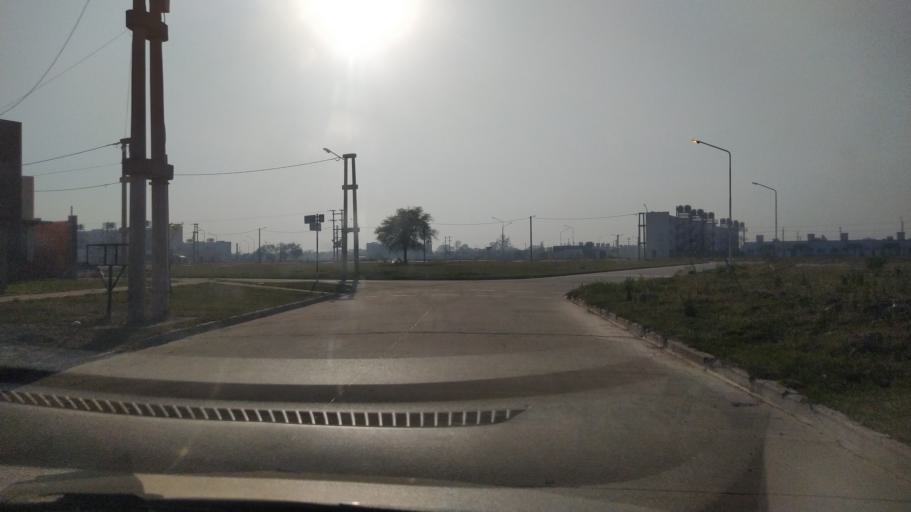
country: AR
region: Corrientes
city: Corrientes
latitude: -27.5265
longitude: -58.8068
